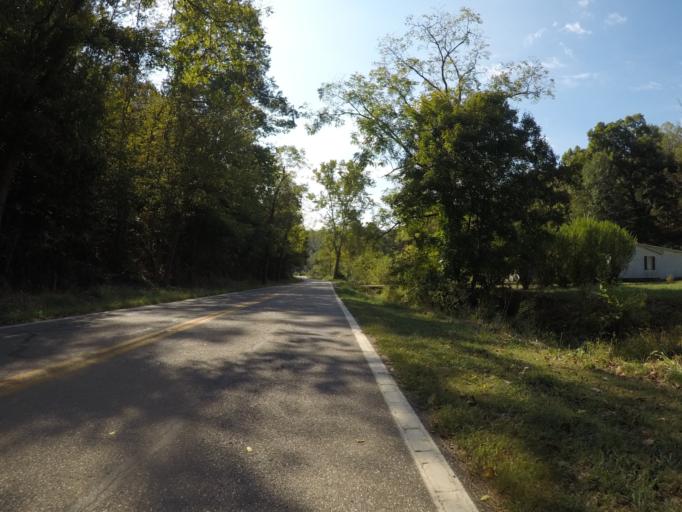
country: US
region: West Virginia
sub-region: Cabell County
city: Lesage
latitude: 38.6387
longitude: -82.4324
